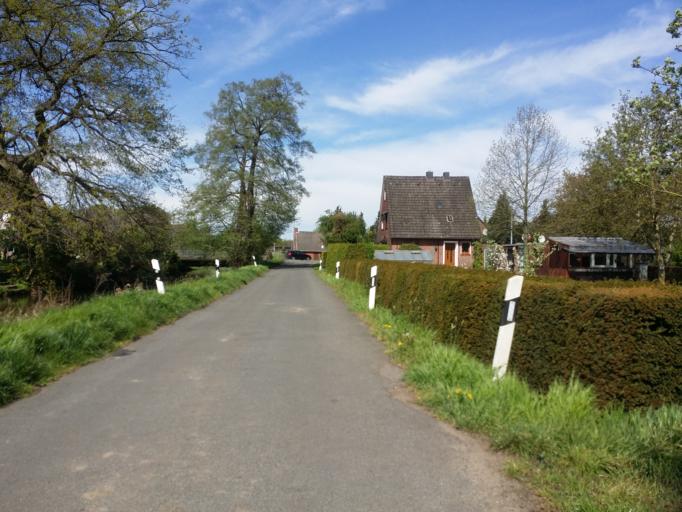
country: DE
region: Lower Saxony
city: Delmenhorst
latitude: 53.0685
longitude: 8.6551
